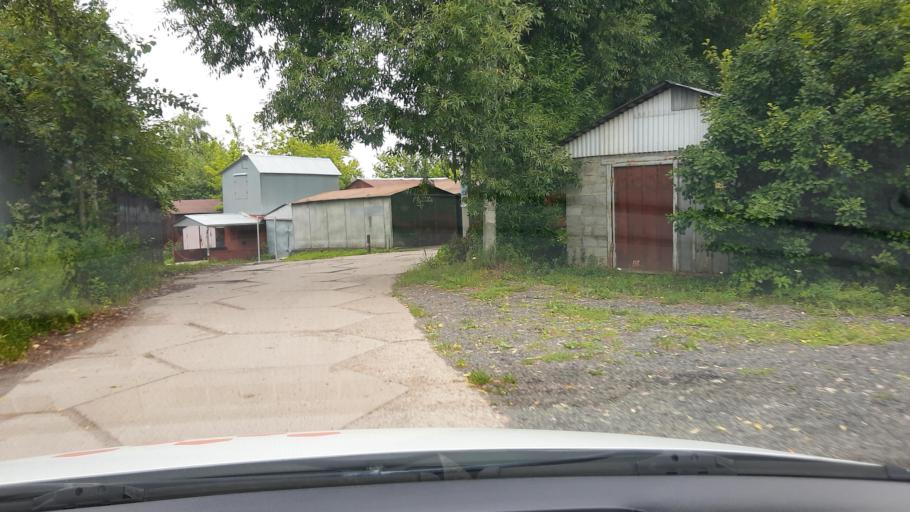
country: RU
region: Moskovskaya
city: Gorki-Leninskiye
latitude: 55.4979
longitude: 37.8257
